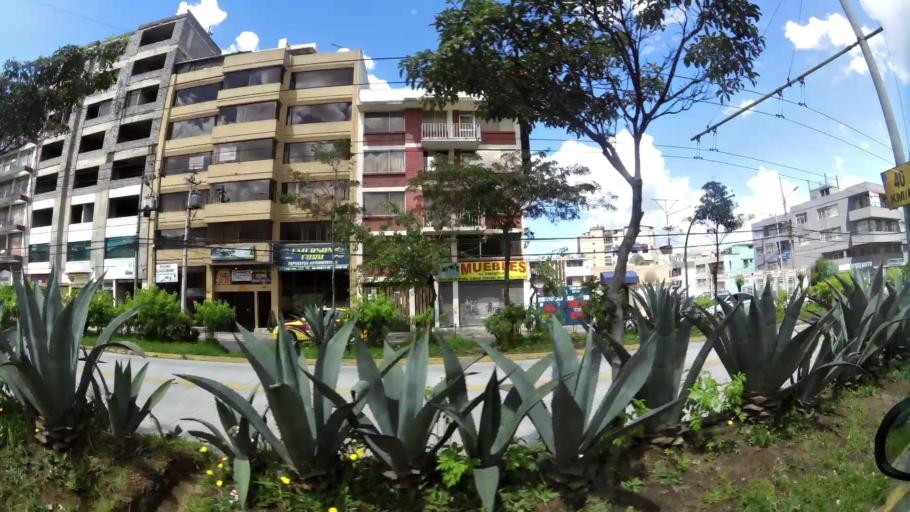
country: EC
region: Pichincha
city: Quito
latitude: -0.1927
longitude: -78.4938
